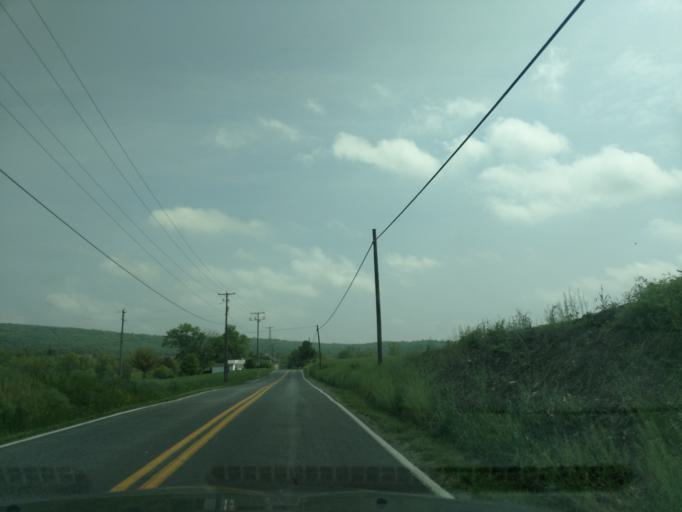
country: US
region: Pennsylvania
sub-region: Chester County
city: Elverson
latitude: 40.2141
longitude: -75.8457
